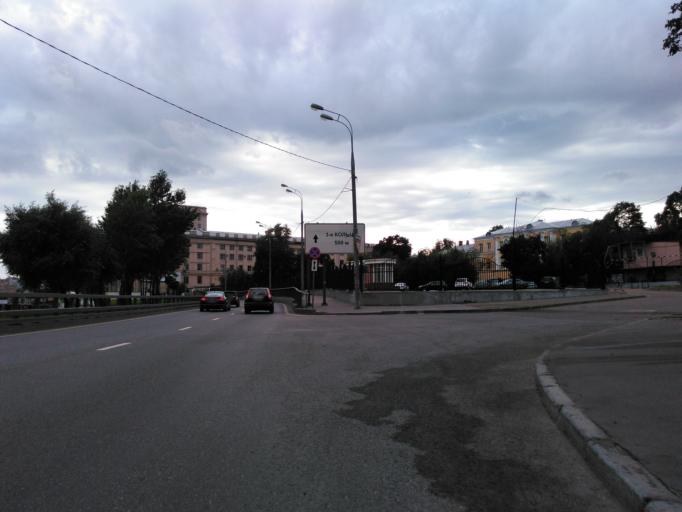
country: RU
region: Moscow
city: Lefortovo
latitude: 55.7683
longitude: 37.6891
